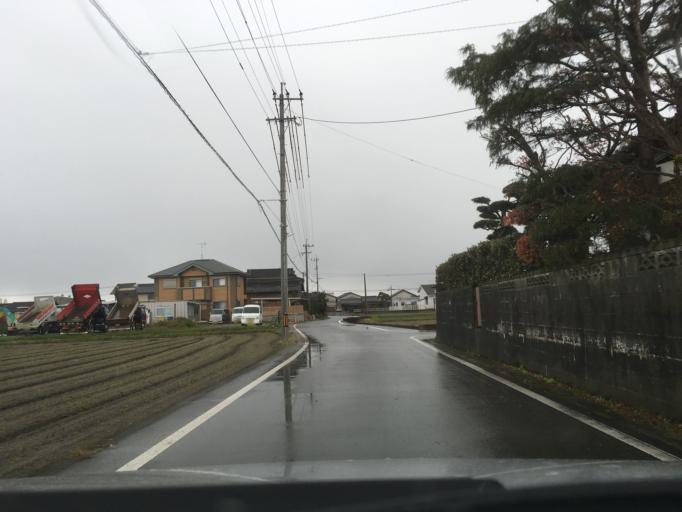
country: JP
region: Saga Prefecture
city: Tosu
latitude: 33.3761
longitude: 130.5726
